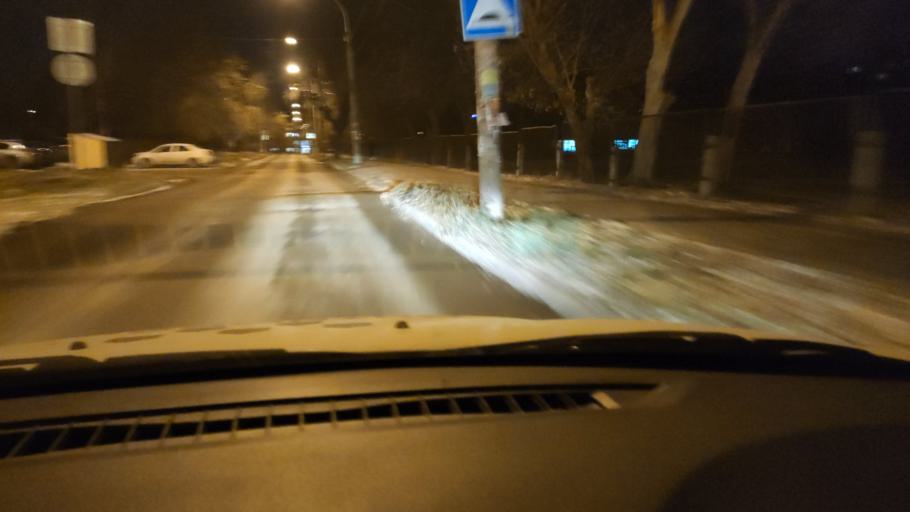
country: RU
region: Perm
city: Perm
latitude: 57.9756
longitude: 56.2365
